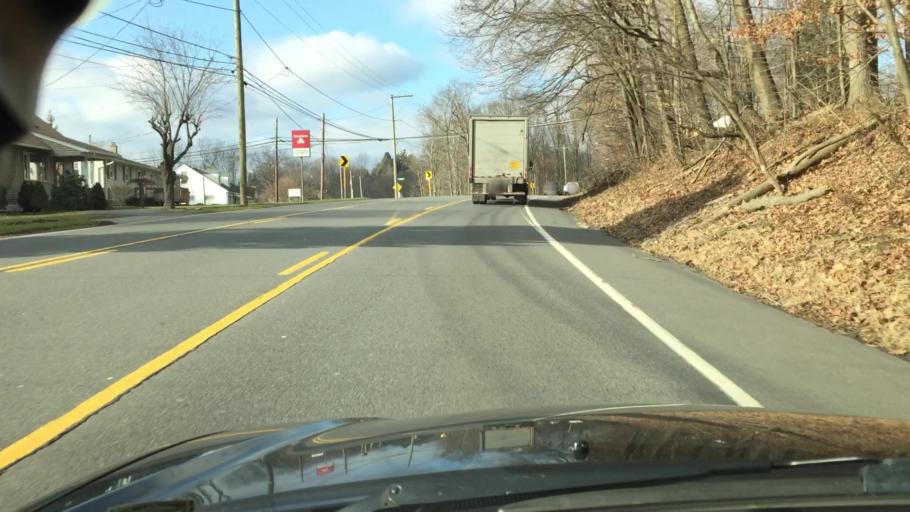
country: US
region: Pennsylvania
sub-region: Luzerne County
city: Dallas
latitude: 41.3360
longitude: -75.9579
